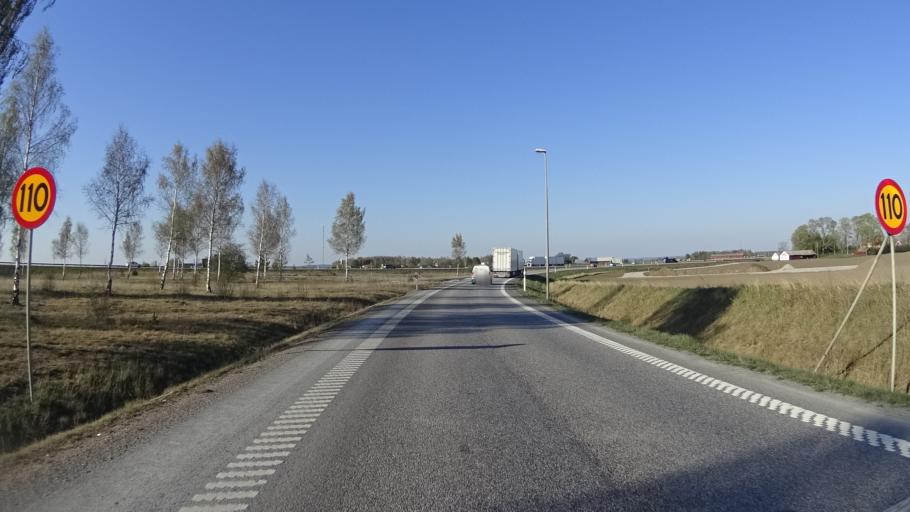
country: SE
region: OEstergoetland
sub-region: Linkopings Kommun
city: Malmslatt
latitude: 58.4343
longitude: 15.5338
